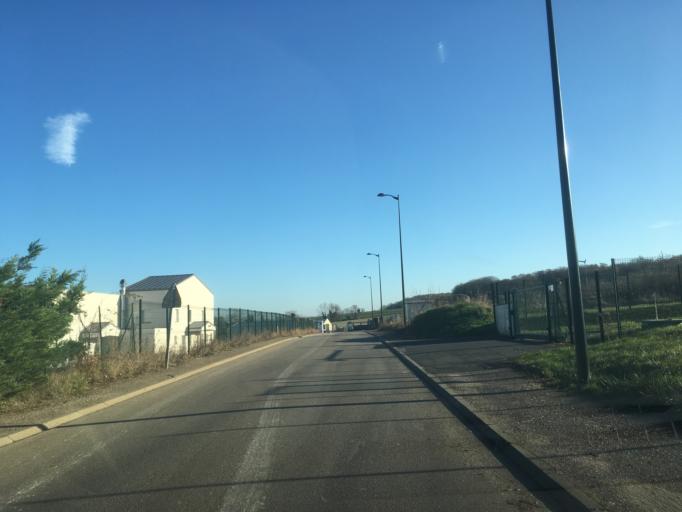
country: FR
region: Haute-Normandie
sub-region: Departement de l'Eure
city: Vernon
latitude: 49.0780
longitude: 1.4990
